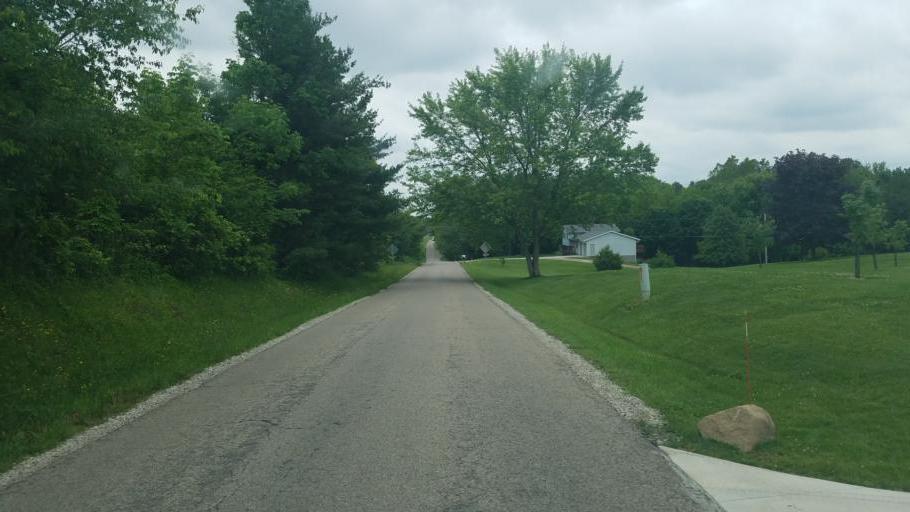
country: US
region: Ohio
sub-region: Licking County
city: Granville South
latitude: 39.9950
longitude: -82.5777
